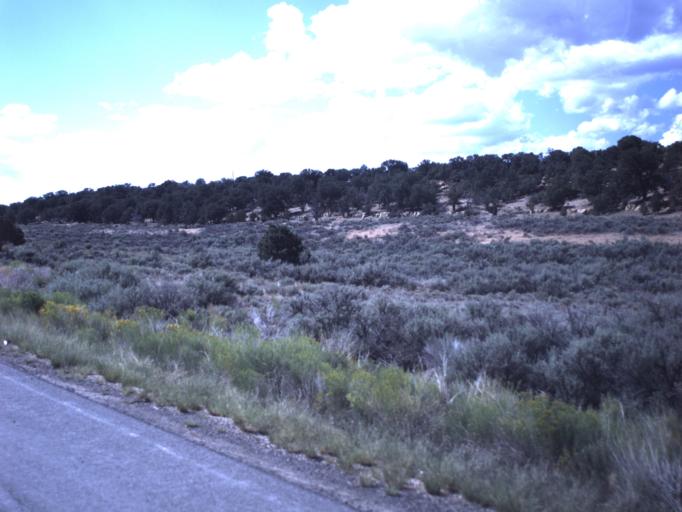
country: US
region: Utah
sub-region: Duchesne County
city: Duchesne
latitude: 40.1805
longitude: -110.6211
